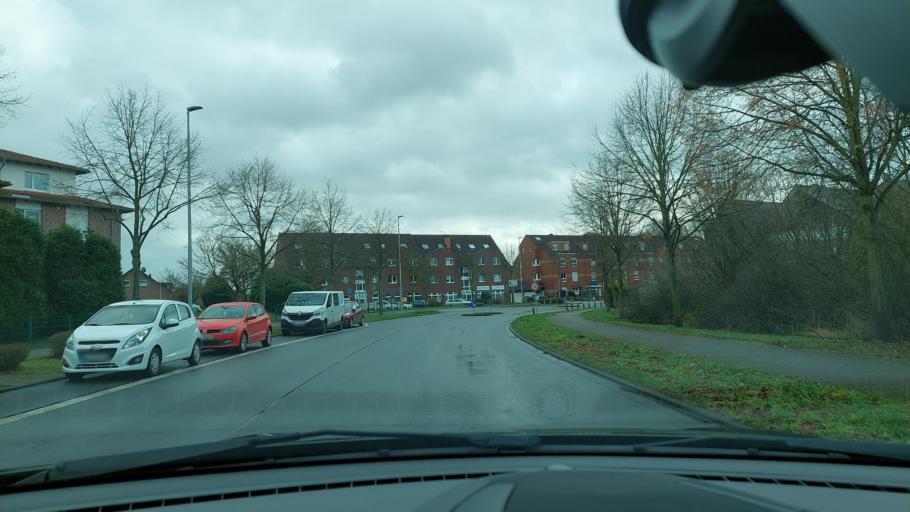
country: DE
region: North Rhine-Westphalia
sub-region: Regierungsbezirk Dusseldorf
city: Dormagen
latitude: 51.0708
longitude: 6.8069
